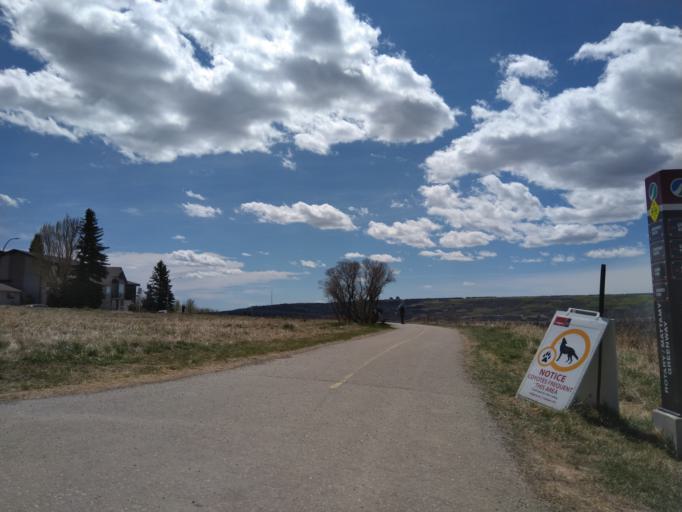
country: CA
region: Alberta
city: Calgary
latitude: 51.1006
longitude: -114.1906
